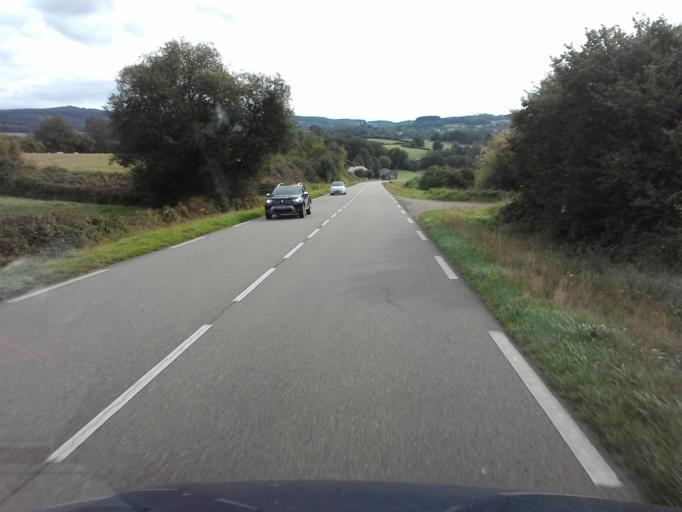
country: FR
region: Bourgogne
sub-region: Departement de la Nievre
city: Chateau-Chinon(Ville)
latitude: 47.0502
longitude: 3.9553
